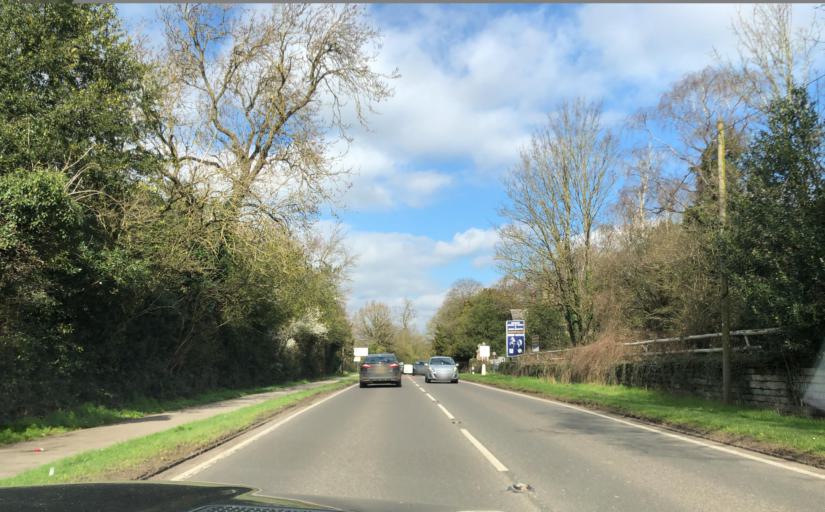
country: GB
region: England
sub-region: Warwickshire
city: Warwick
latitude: 52.2964
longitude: -1.5761
